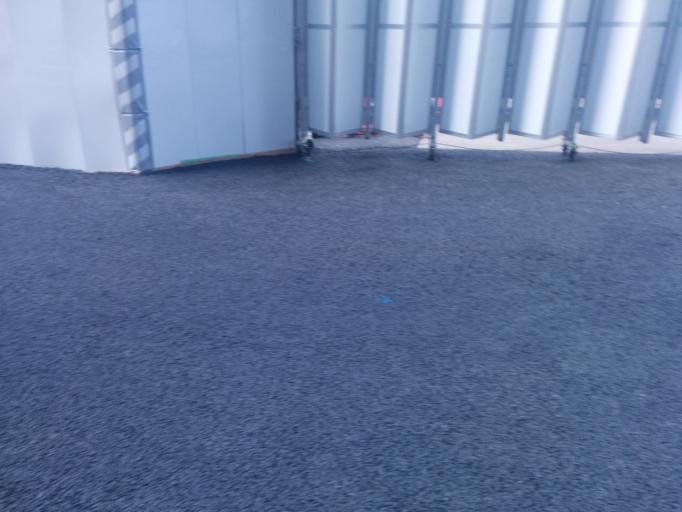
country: JP
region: Tokyo
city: Tokyo
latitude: 35.6922
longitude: 139.6880
